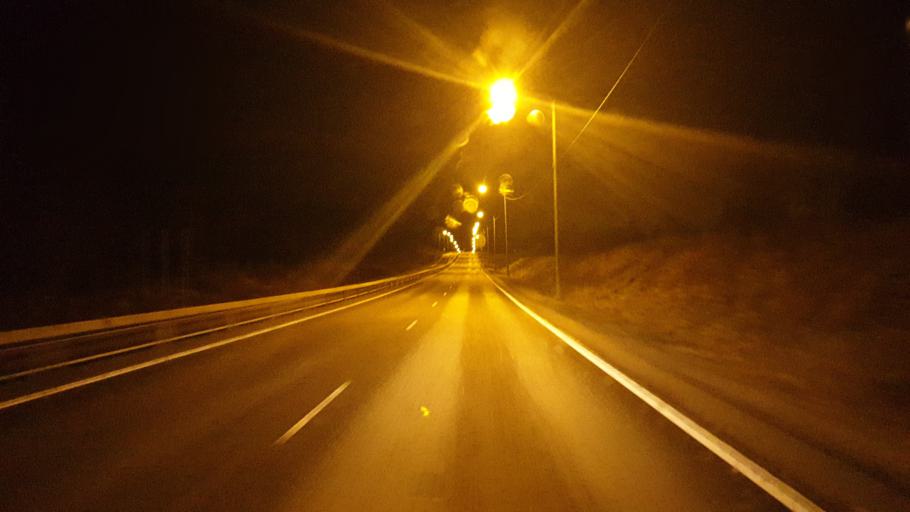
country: FI
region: Central Finland
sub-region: AEaenekoski
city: AEaenekoski
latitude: 62.5347
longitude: 25.6820
